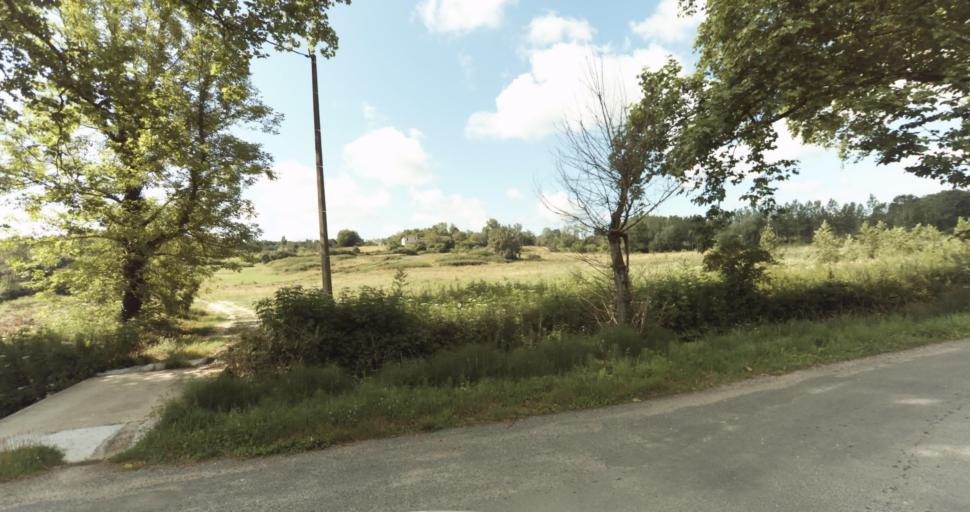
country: FR
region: Aquitaine
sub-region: Departement de la Gironde
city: Bazas
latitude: 44.4343
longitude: -0.1986
